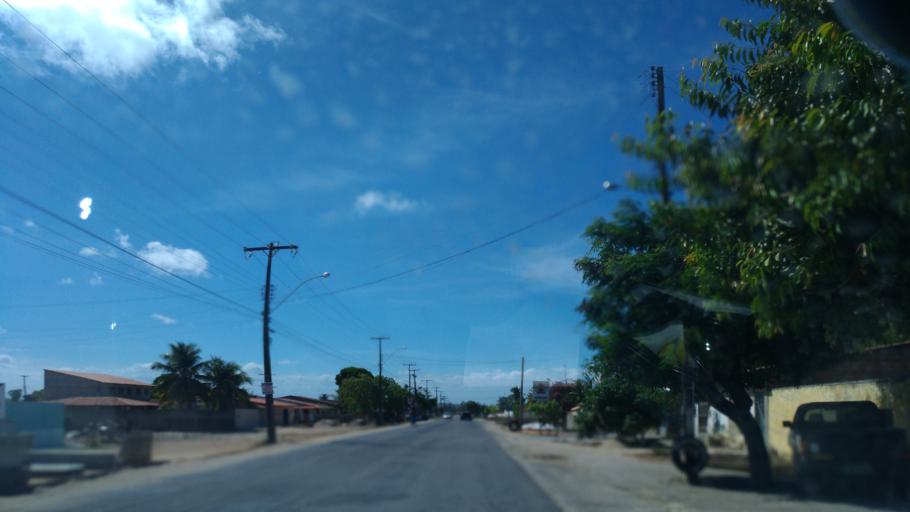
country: BR
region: Alagoas
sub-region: Marechal Deodoro
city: Marechal Deodoro
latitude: -9.7492
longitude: -35.8765
